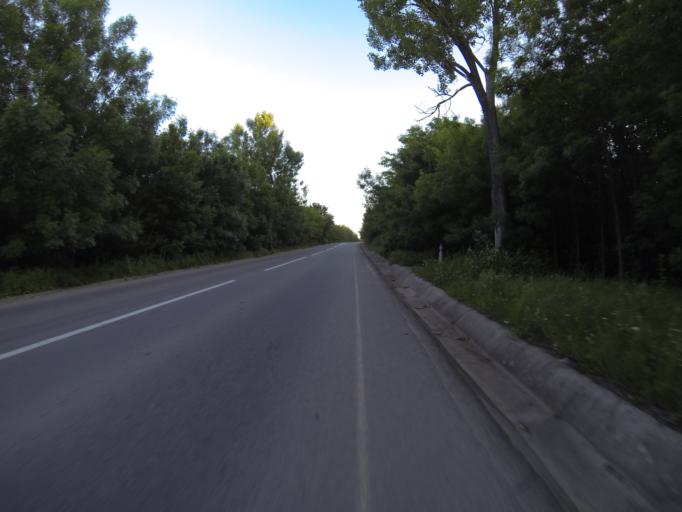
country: RO
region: Dolj
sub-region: Comuna Caloparu
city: Calopar
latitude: 44.1558
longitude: 23.7436
